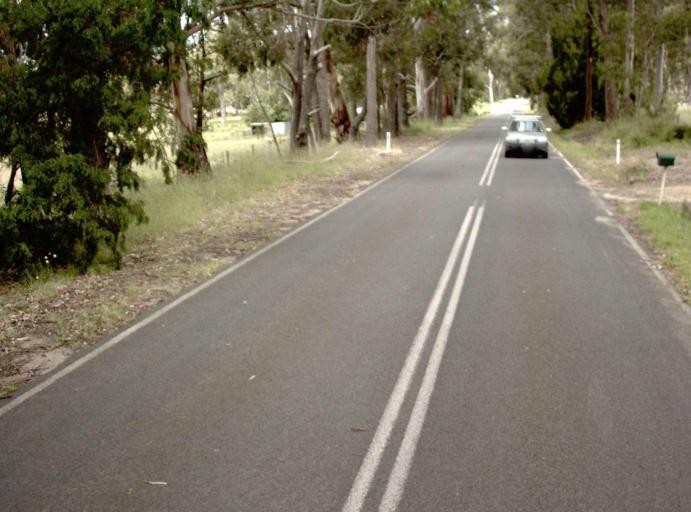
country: AU
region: Victoria
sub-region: Latrobe
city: Traralgon
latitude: -38.5026
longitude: 146.6483
